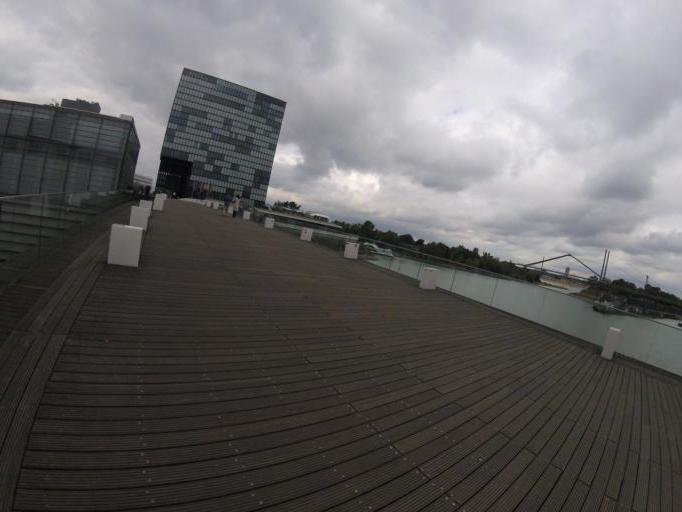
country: DE
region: North Rhine-Westphalia
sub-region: Regierungsbezirk Dusseldorf
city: Dusseldorf
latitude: 51.2155
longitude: 6.7542
